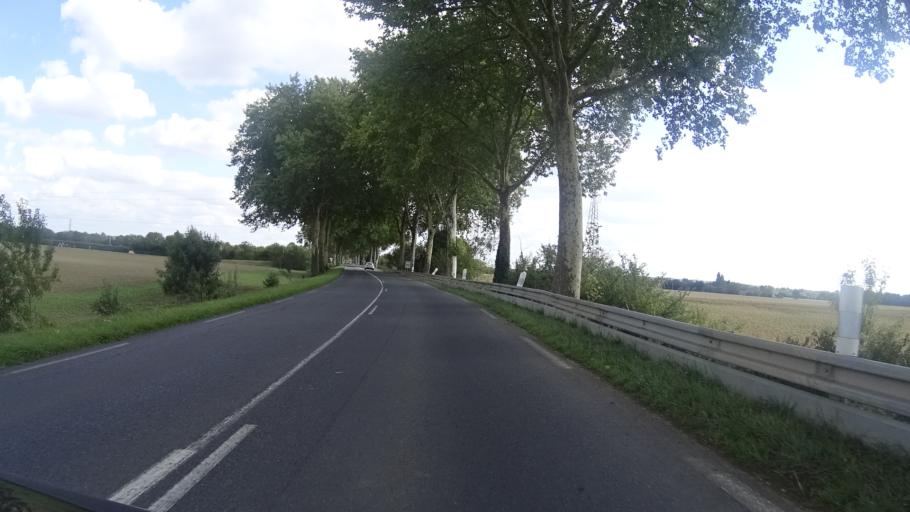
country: FR
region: Pays de la Loire
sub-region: Departement de Maine-et-Loire
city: Juigne-sur-Loire
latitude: 47.4244
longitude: -0.4675
